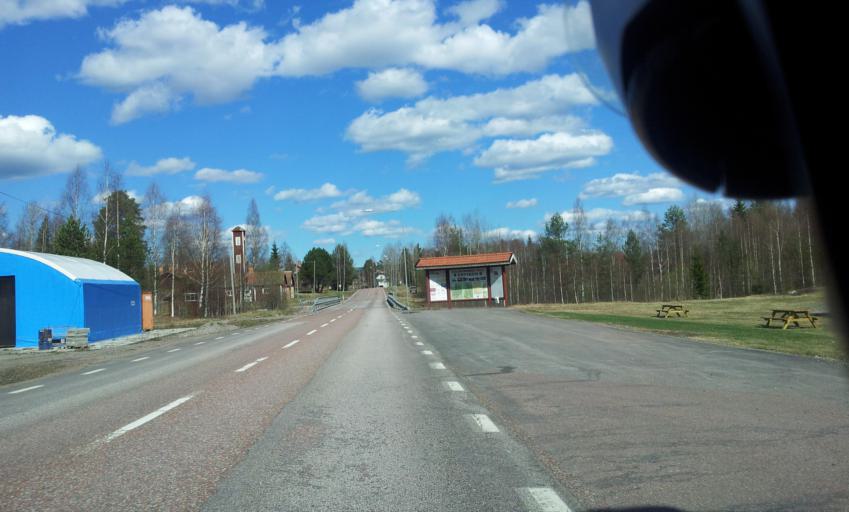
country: SE
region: Dalarna
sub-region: Faluns Kommun
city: Svardsjo
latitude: 60.8030
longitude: 15.7540
